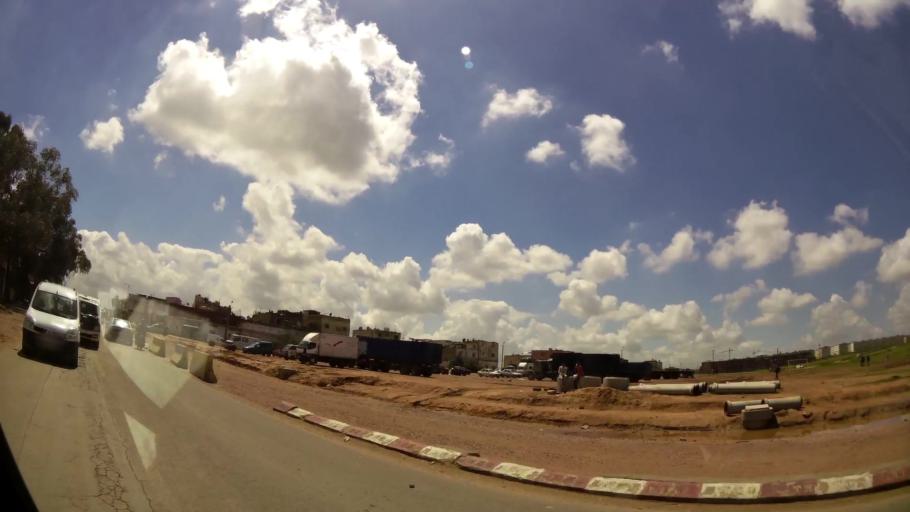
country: MA
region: Grand Casablanca
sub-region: Mediouna
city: Tit Mellil
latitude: 33.5406
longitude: -7.5415
